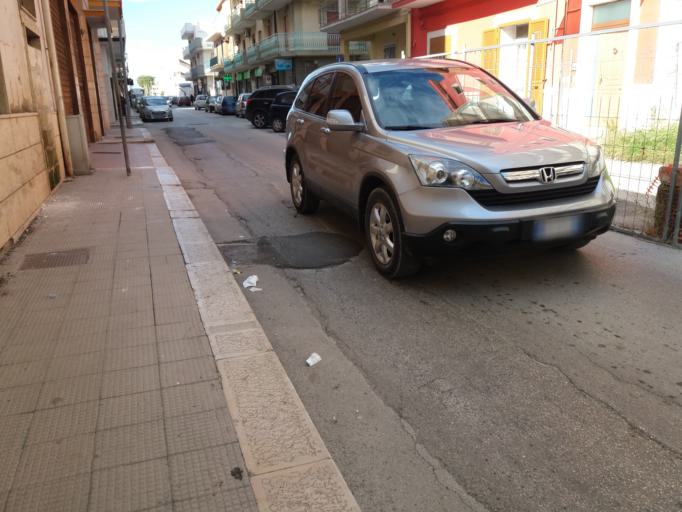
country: IT
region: Apulia
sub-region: Provincia di Bari
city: Bitonto
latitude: 41.1102
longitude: 16.6832
